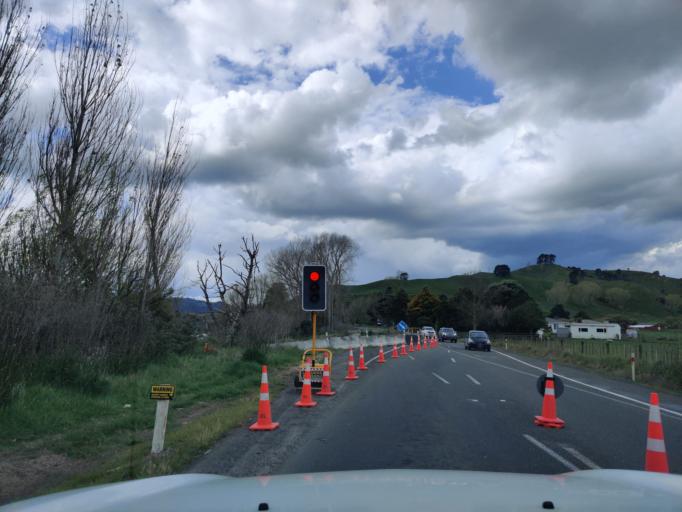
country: NZ
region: Manawatu-Wanganui
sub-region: Wanganui District
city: Wanganui
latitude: -39.8764
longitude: 175.1101
